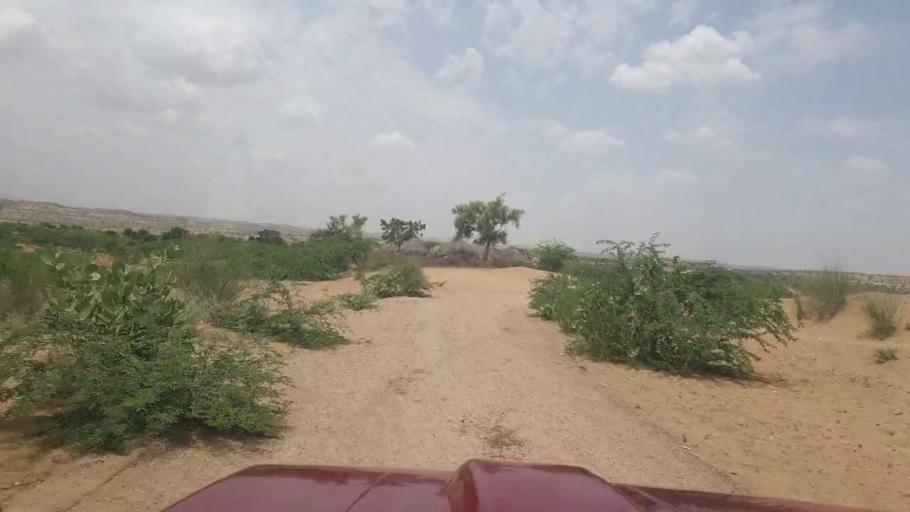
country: PK
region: Sindh
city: Islamkot
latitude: 25.2279
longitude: 70.5069
